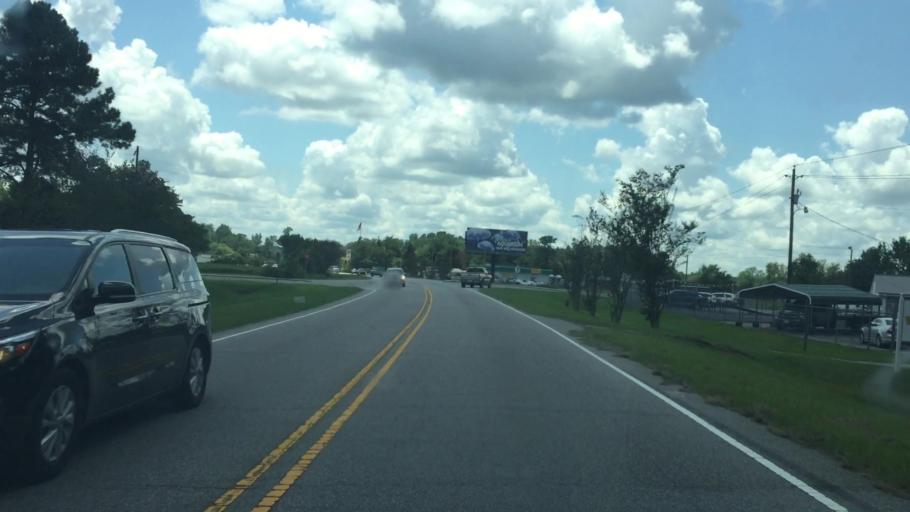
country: US
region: North Carolina
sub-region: Columbus County
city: Tabor City
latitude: 34.1358
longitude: -78.8744
